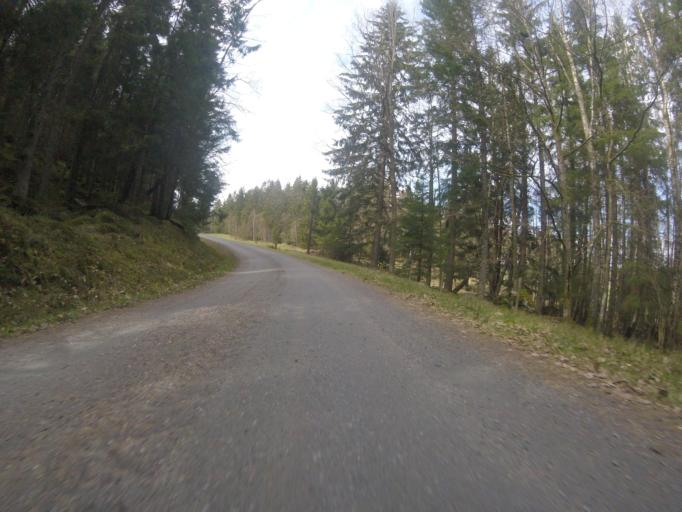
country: SE
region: Vaestra Goetaland
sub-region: Alingsas Kommun
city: Ingared
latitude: 57.8691
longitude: 12.5157
